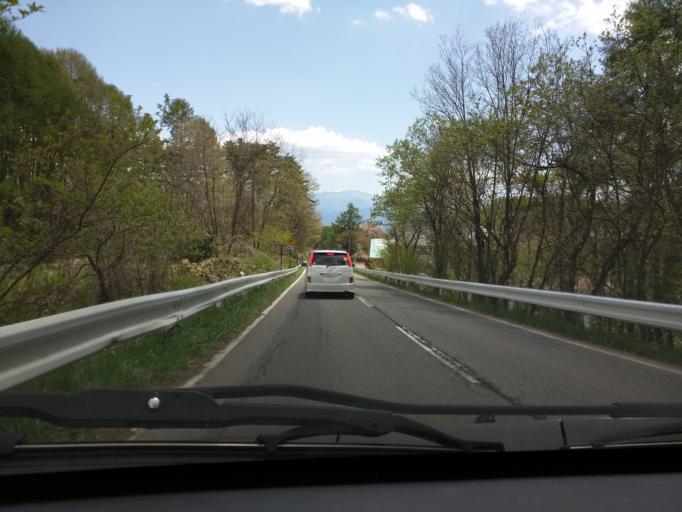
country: JP
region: Nagano
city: Nagano-shi
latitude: 36.7039
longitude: 138.1475
